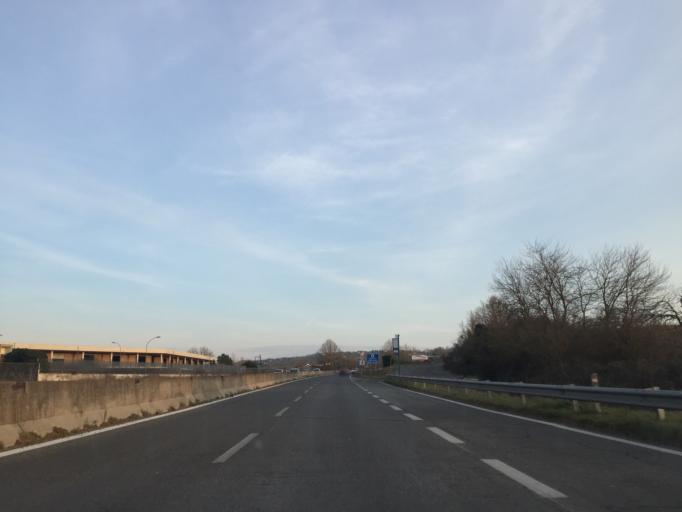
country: IT
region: Latium
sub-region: Citta metropolitana di Roma Capitale
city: Campagnano di Roma
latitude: 42.1539
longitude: 12.3457
